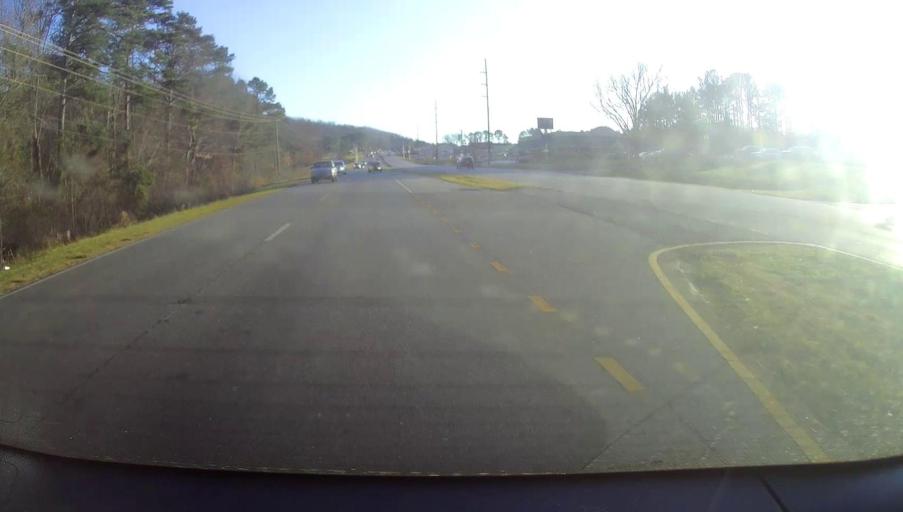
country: US
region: Alabama
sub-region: Calhoun County
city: Saks
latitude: 33.6919
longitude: -85.8232
